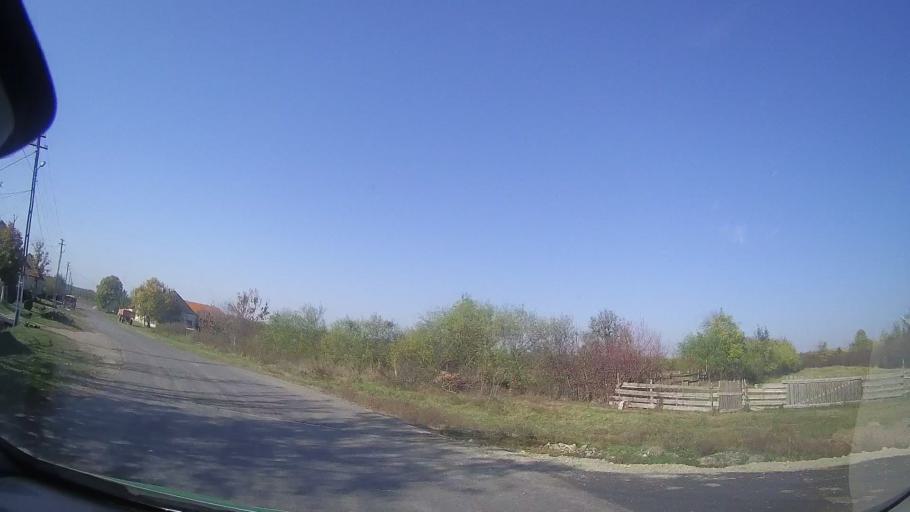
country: RO
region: Timis
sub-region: Comuna Ghizela
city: Ghizela
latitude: 45.8215
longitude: 21.7406
